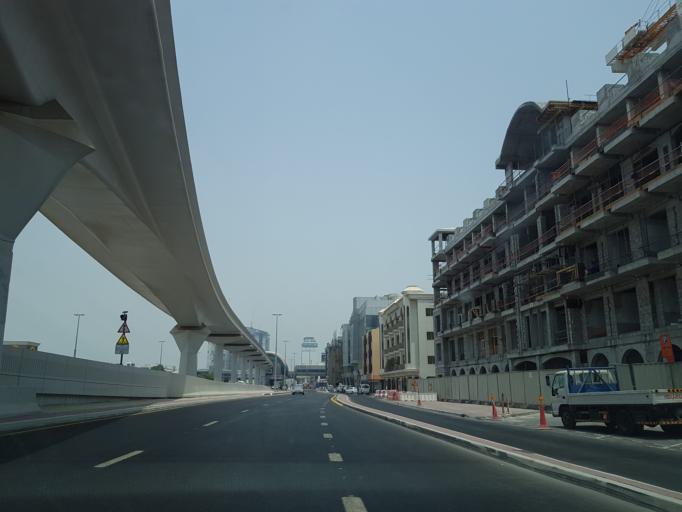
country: AE
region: Ash Shariqah
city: Sharjah
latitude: 25.2408
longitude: 55.2963
